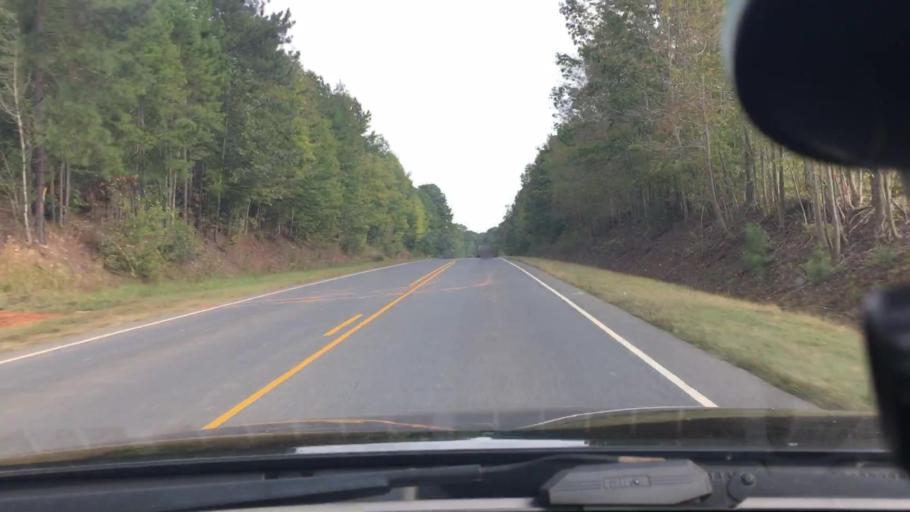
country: US
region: North Carolina
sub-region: Montgomery County
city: Mount Gilead
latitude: 35.3069
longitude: -80.0378
